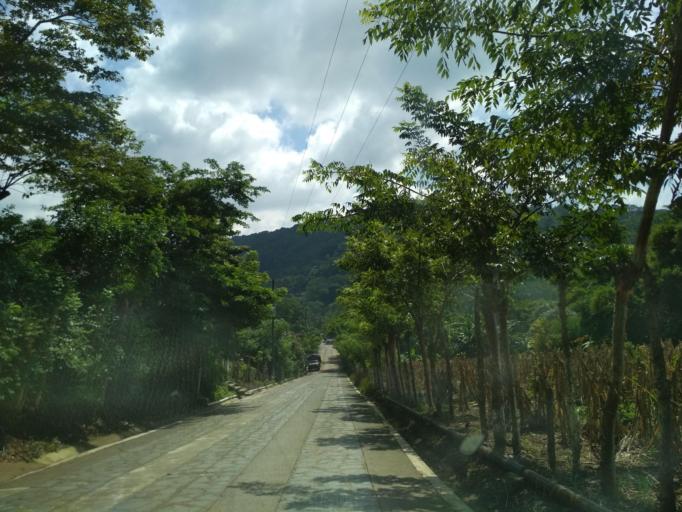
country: MX
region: Veracruz
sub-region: San Andres Tuxtla
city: Texcaltitan Xoteapan (Texcaltitan)
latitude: 18.4454
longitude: -95.2522
